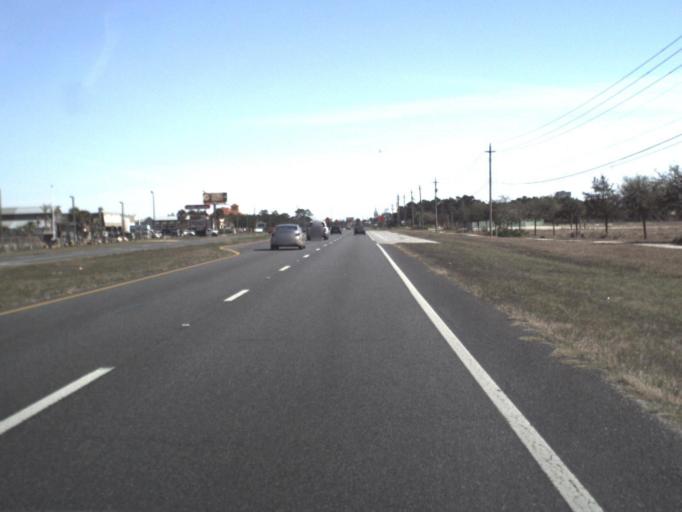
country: US
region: Florida
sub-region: Bay County
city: Laguna Beach
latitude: 30.2395
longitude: -85.9113
